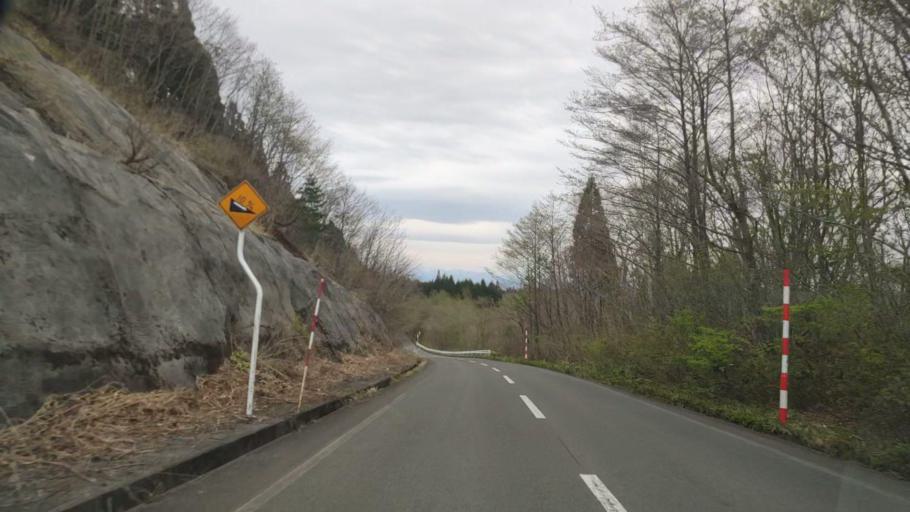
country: JP
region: Akita
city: Hanawa
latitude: 40.4002
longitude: 140.8016
